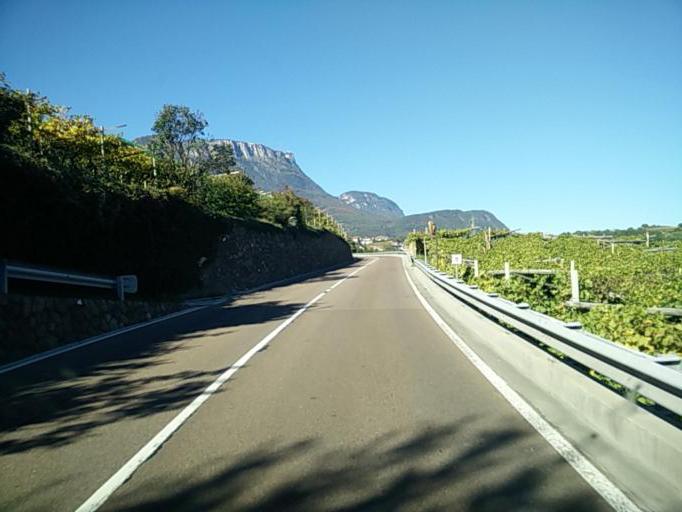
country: IT
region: Trentino-Alto Adige
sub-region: Bolzano
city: Caldaro sulla Strada del Vino
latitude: 46.3982
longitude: 11.2522
